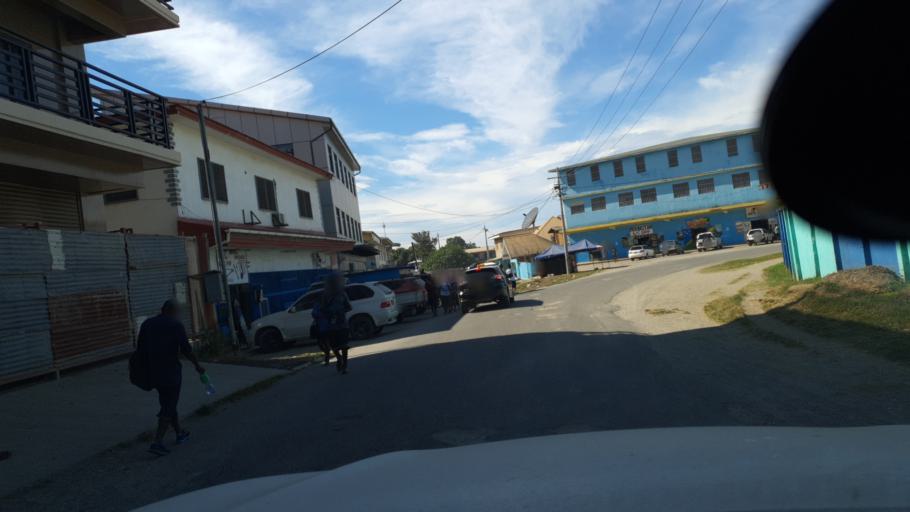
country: SB
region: Guadalcanal
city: Honiara
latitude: -9.4373
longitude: 159.9669
